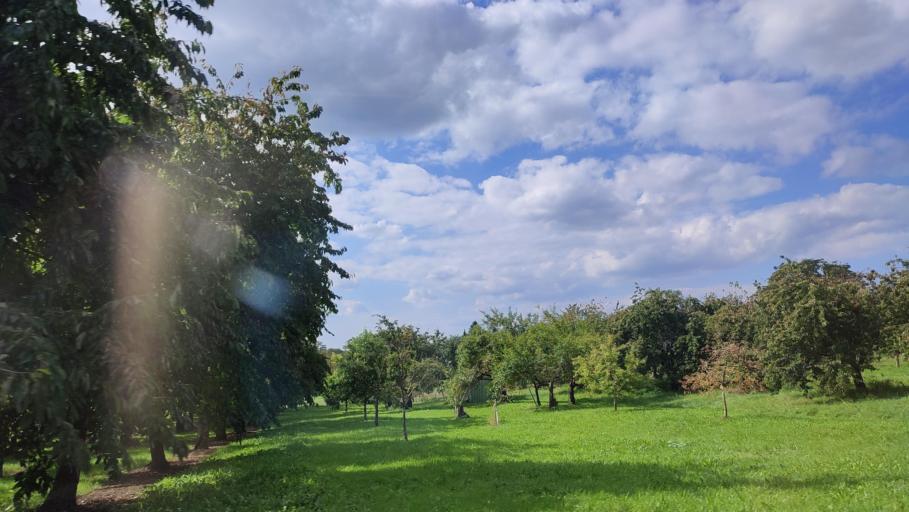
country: DE
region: Baden-Wuerttemberg
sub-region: Freiburg Region
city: Appenweier
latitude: 48.5233
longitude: 8.0062
